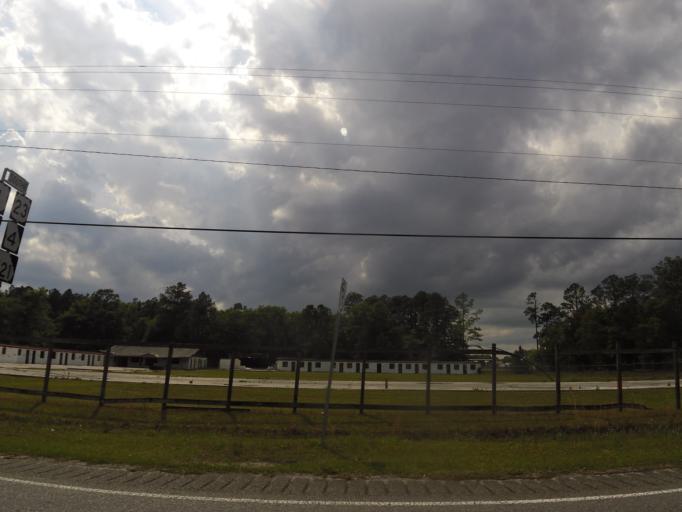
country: US
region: Georgia
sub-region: Charlton County
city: Folkston
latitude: 30.8592
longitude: -82.0111
